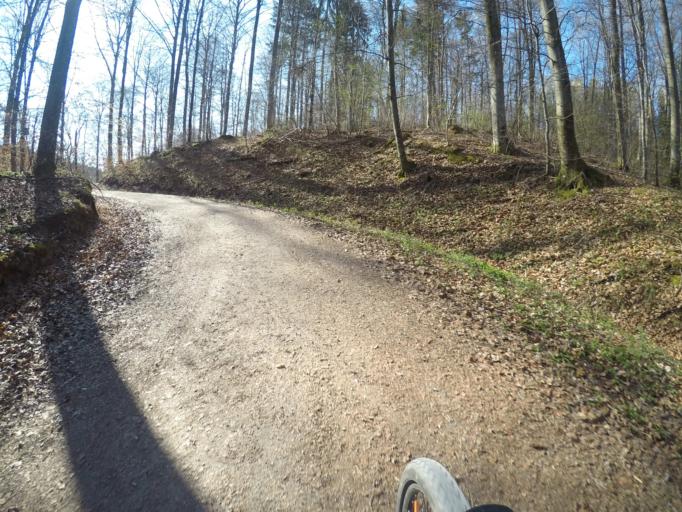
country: DE
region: Baden-Wuerttemberg
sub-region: Tuebingen Region
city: Dettenhausen
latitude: 48.6055
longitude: 9.1082
